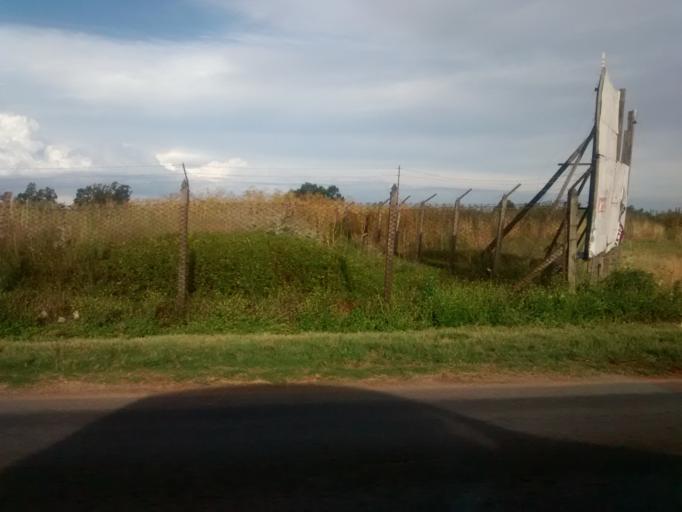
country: AR
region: Buenos Aires
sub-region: Partido de Loberia
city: Loberia
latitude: -38.2051
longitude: -58.7355
